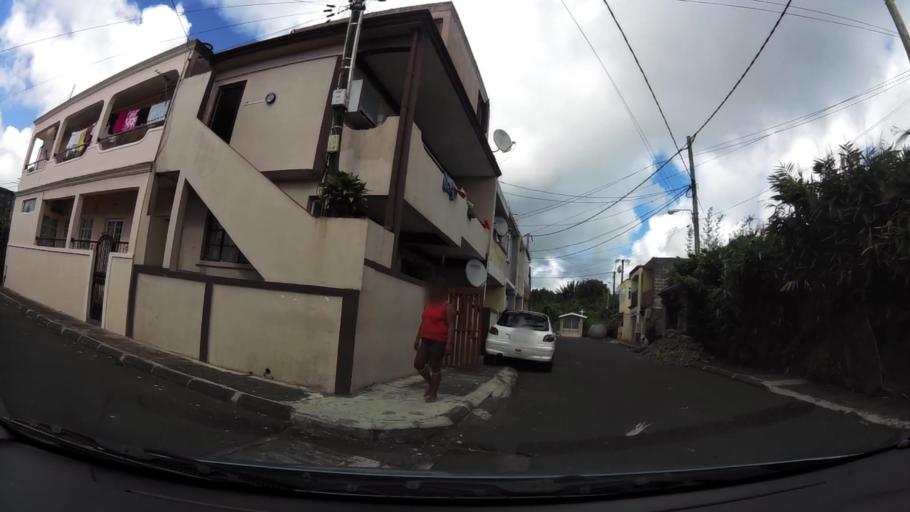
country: MU
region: Plaines Wilhems
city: Curepipe
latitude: -20.3335
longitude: 57.5289
